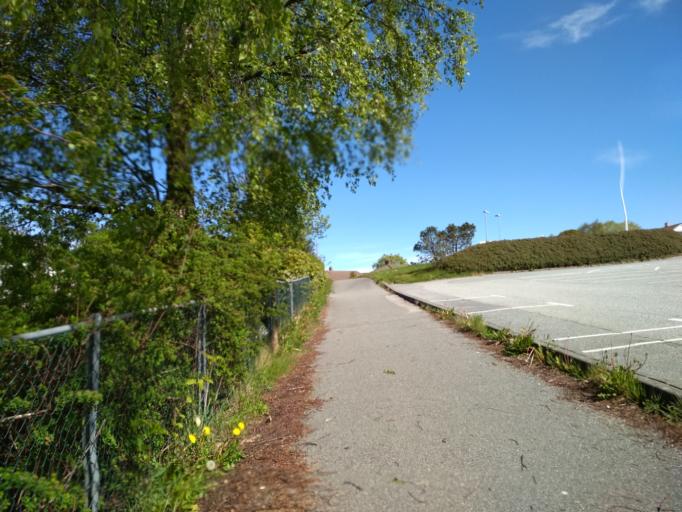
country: NO
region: Rogaland
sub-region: Stavanger
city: Stavanger
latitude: 58.9534
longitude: 5.7375
